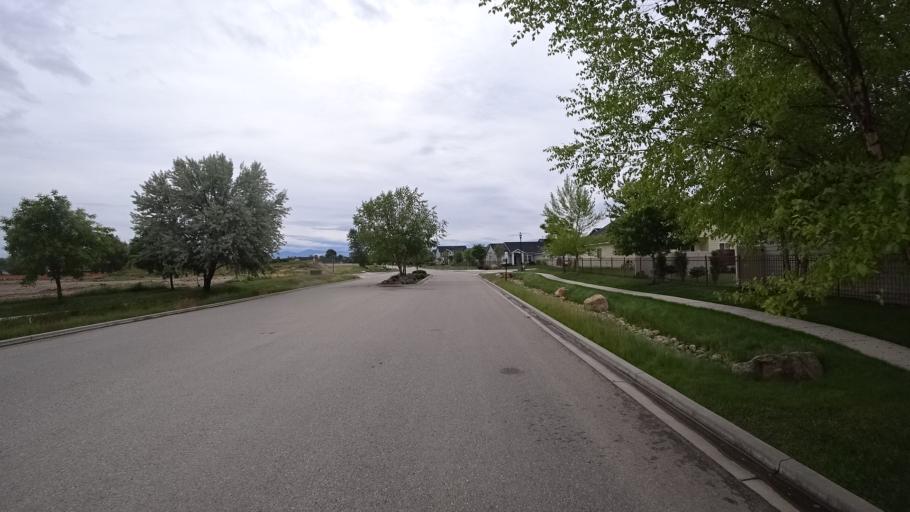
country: US
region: Idaho
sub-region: Ada County
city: Star
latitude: 43.7013
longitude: -116.4986
